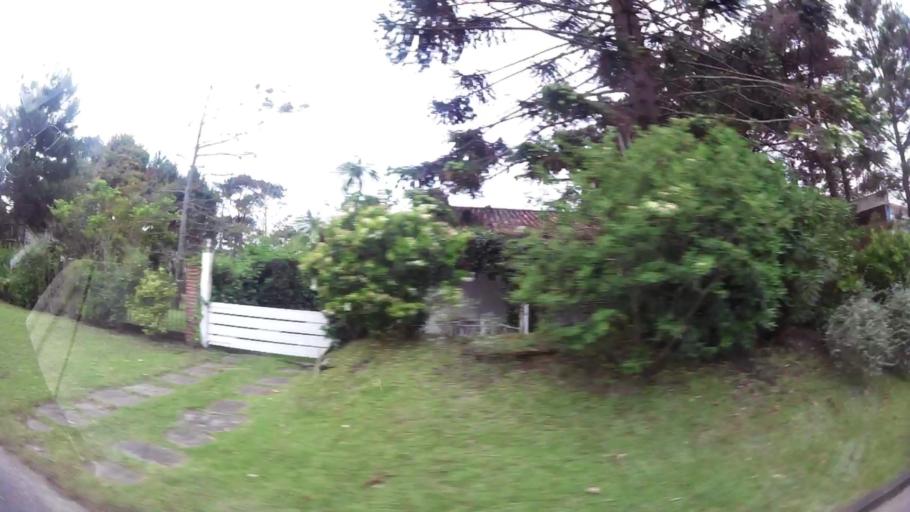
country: UY
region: Maldonado
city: Punta del Este
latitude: -34.9429
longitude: -54.9400
